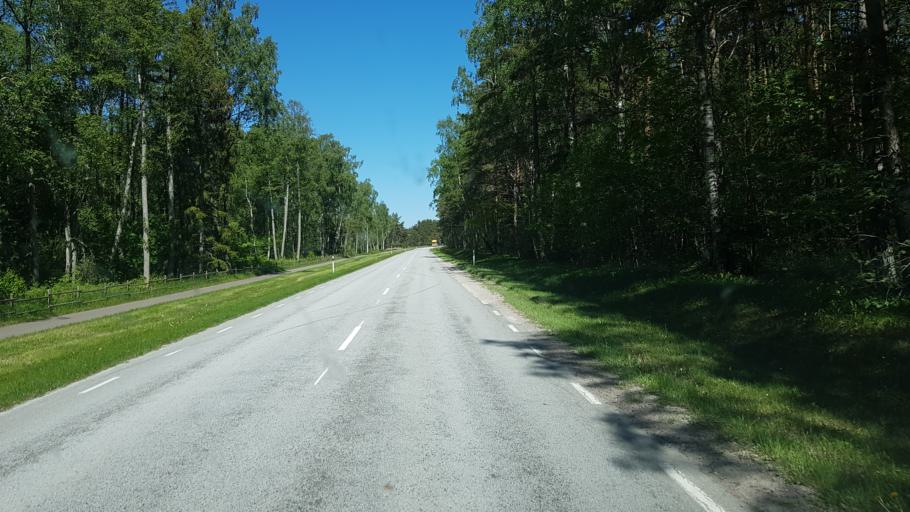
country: EE
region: Saare
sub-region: Kuressaare linn
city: Kuressaare
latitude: 58.1886
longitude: 22.2645
